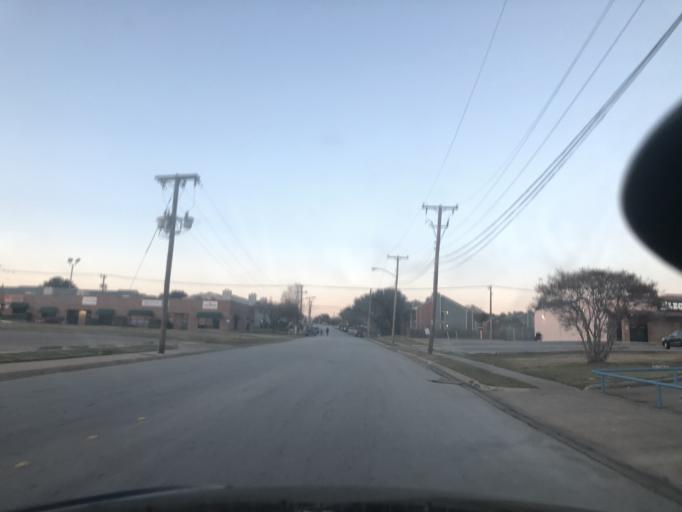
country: US
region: Texas
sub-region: Tarrant County
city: White Settlement
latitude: 32.7247
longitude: -97.4691
